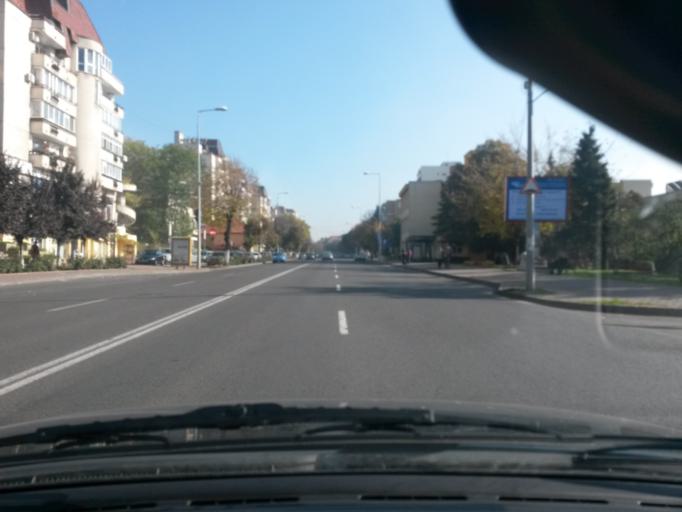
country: RO
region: Mures
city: Targu-Mures
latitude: 46.5396
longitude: 24.5604
